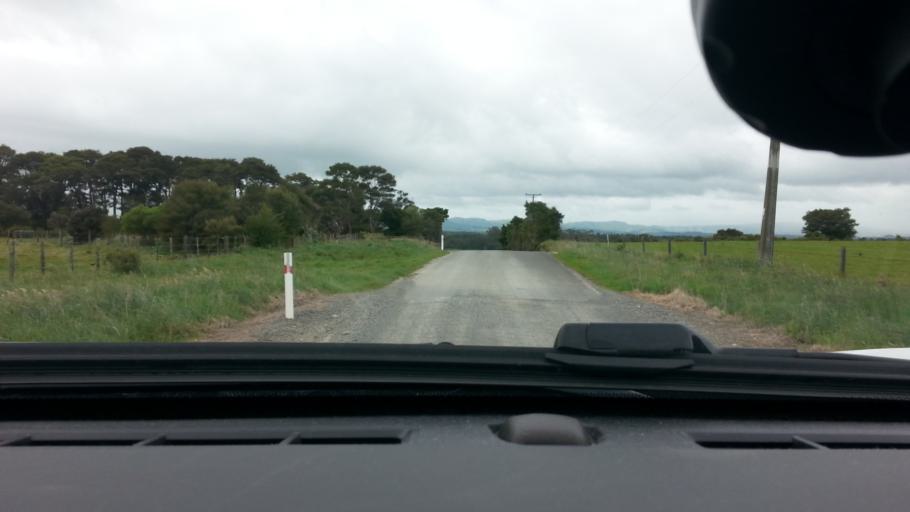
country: NZ
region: Wellington
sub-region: Upper Hutt City
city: Upper Hutt
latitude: -41.0813
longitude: 175.3521
